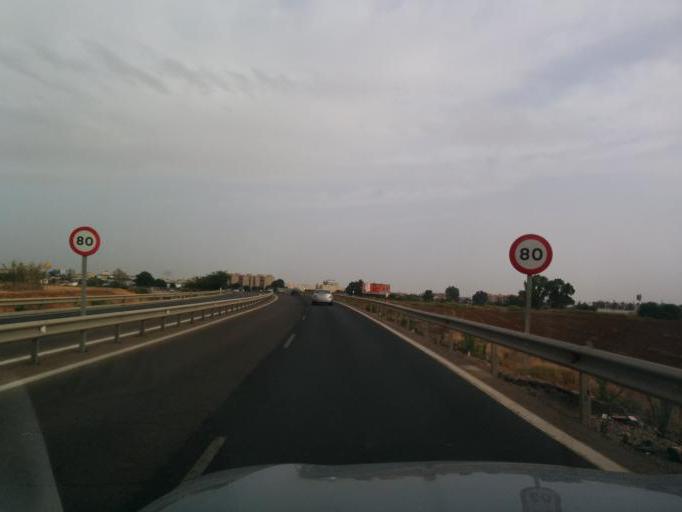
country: ES
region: Andalusia
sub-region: Provincia de Sevilla
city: Sevilla
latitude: 37.4160
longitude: -5.9435
